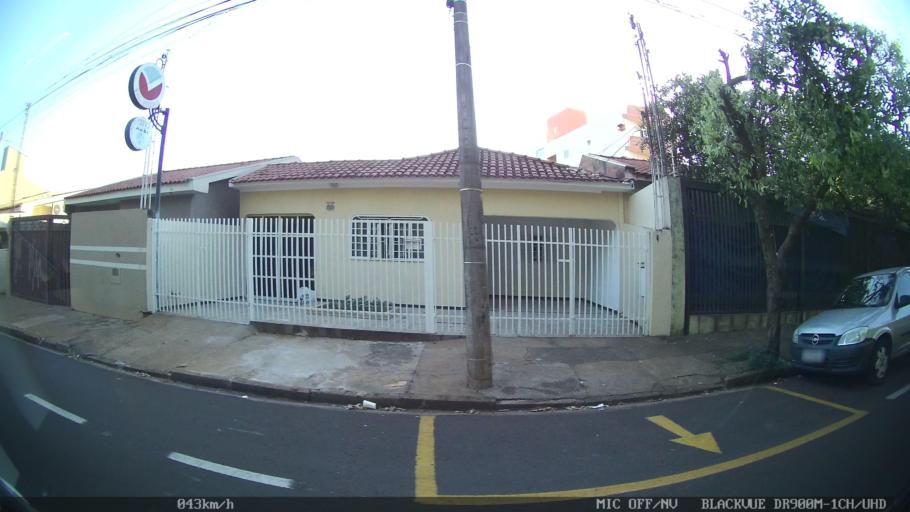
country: BR
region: Sao Paulo
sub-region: Sao Jose Do Rio Preto
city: Sao Jose do Rio Preto
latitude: -20.8007
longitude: -49.3596
